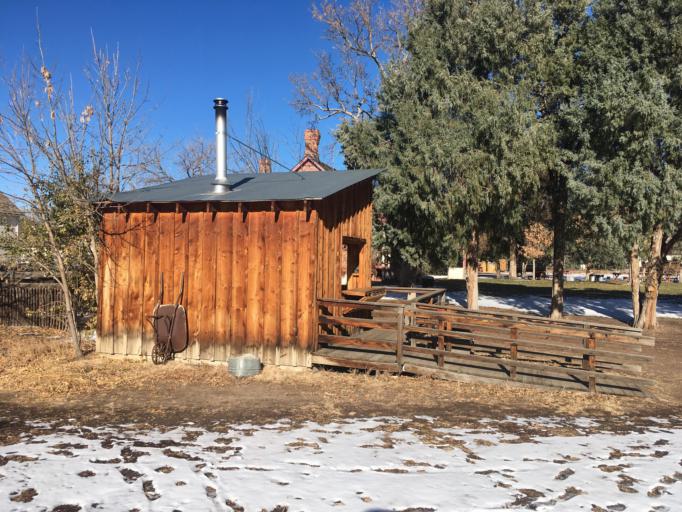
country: US
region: Colorado
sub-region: Arapahoe County
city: Glendale
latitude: 39.7026
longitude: -104.9276
